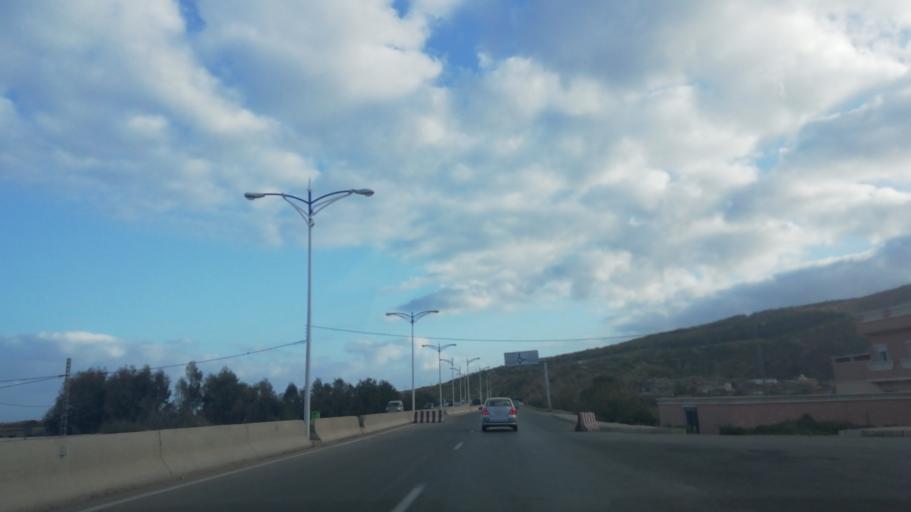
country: DZ
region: Mostaganem
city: Mostaganem
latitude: 36.0324
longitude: 0.1396
